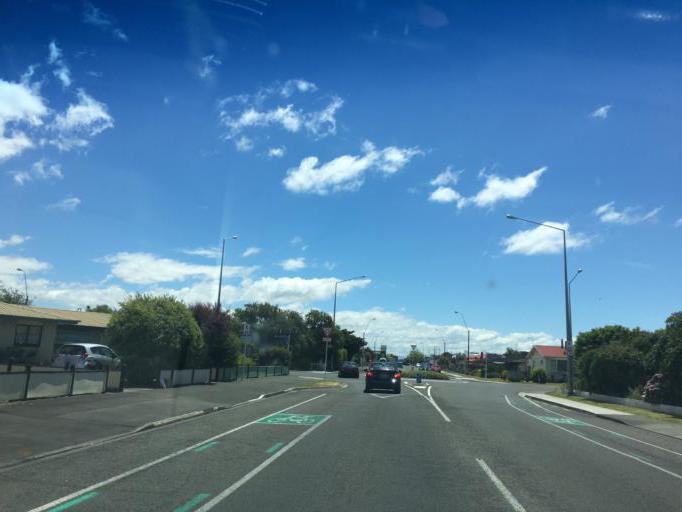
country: NZ
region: Hawke's Bay
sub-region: Hastings District
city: Hastings
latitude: -39.6450
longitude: 176.8519
